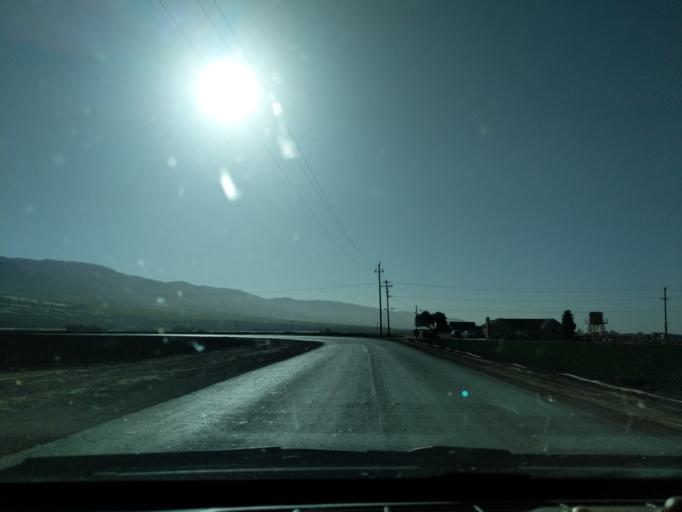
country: US
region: California
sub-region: Monterey County
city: Soledad
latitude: 36.4072
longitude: -121.3570
